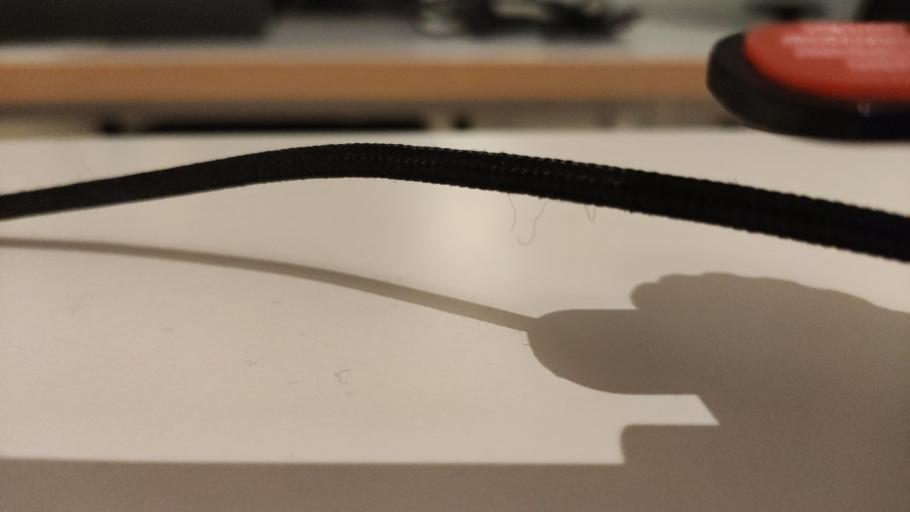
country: RU
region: Moskovskaya
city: Noginsk-9
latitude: 56.1036
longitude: 38.6403
